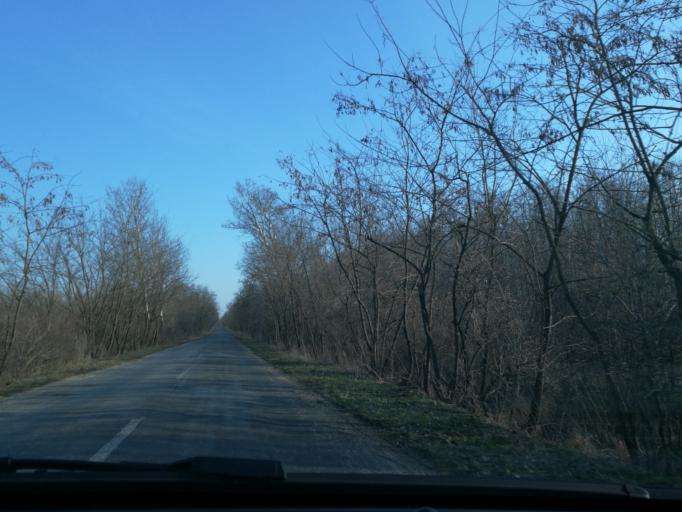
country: HU
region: Szabolcs-Szatmar-Bereg
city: Nyirbogdany
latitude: 48.0306
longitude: 21.9257
